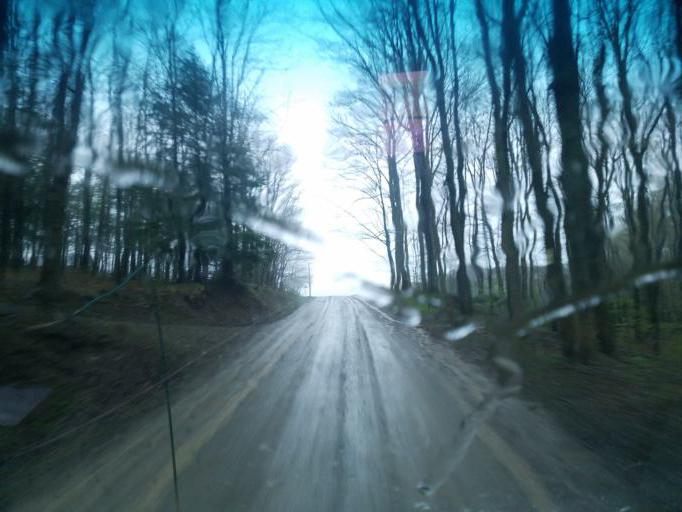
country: US
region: Pennsylvania
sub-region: Tioga County
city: Westfield
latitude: 41.9247
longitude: -77.7214
